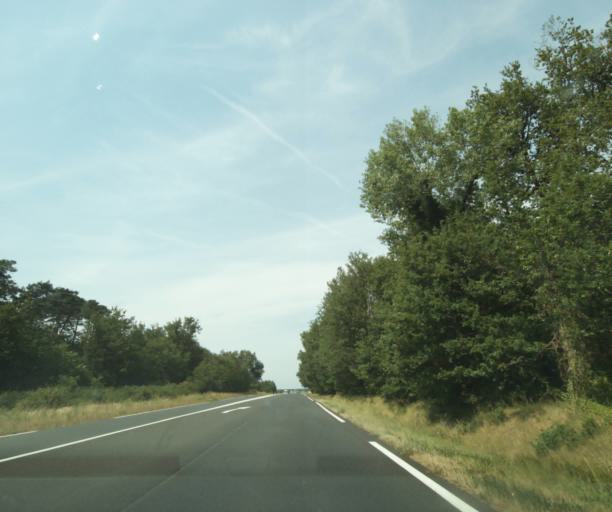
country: FR
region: Centre
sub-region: Departement d'Indre-et-Loire
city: Sainte-Maure-de-Touraine
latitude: 47.0686
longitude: 0.6145
